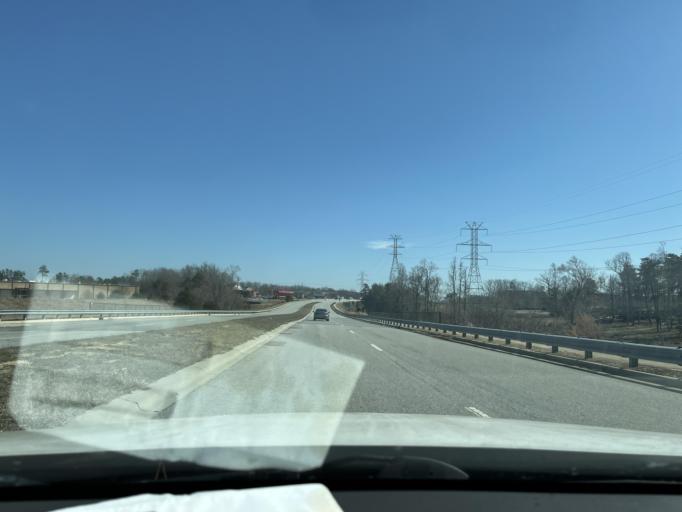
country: US
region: North Carolina
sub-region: Guilford County
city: Jamestown
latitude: 36.0035
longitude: -79.9127
